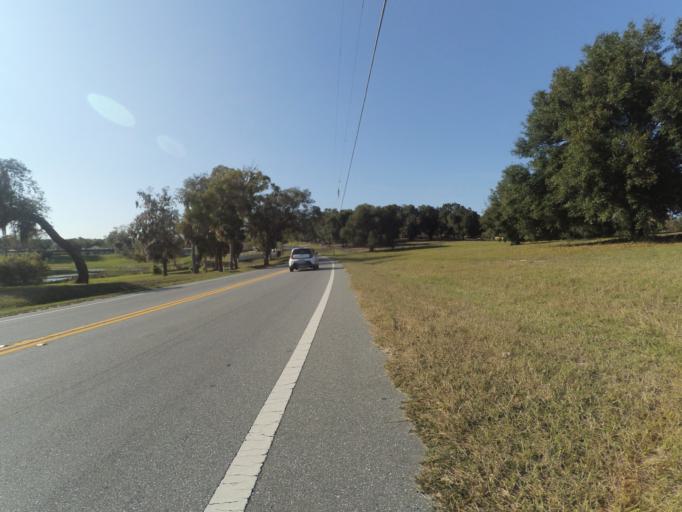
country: US
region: Florida
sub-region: Lake County
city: Umatilla
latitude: 28.9672
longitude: -81.6509
